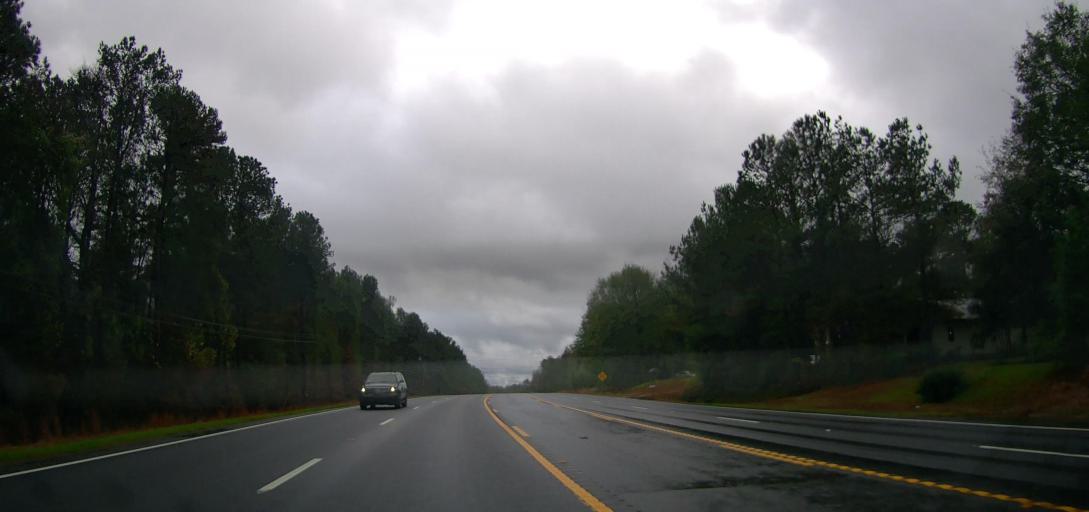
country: US
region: Georgia
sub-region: Clarke County
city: Country Club Estates
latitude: 34.0132
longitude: -83.3877
